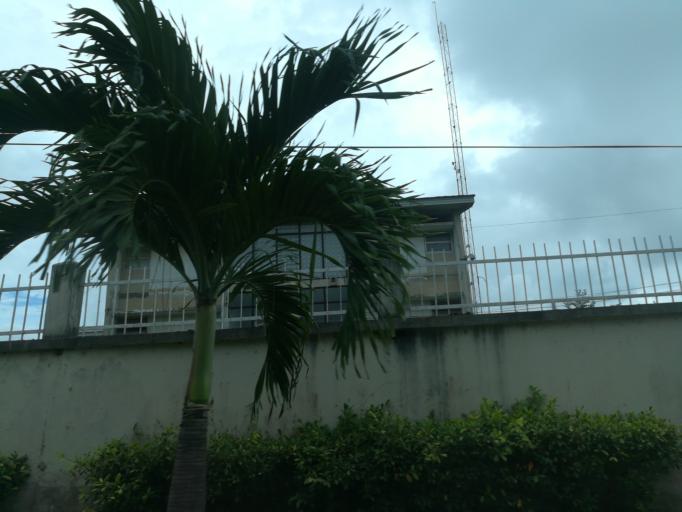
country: NG
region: Lagos
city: Lagos
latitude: 6.4330
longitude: 3.4118
